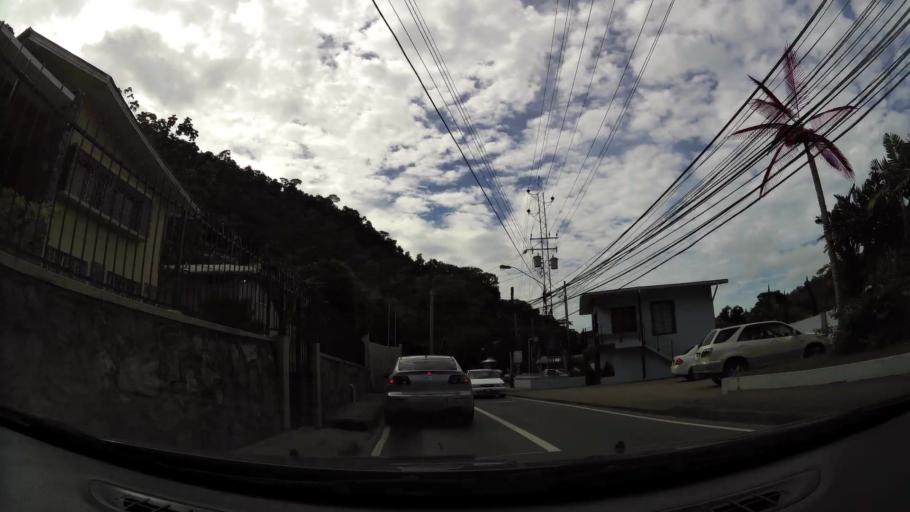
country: TT
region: Diego Martin
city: Petit Valley
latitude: 10.6923
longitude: -61.5181
